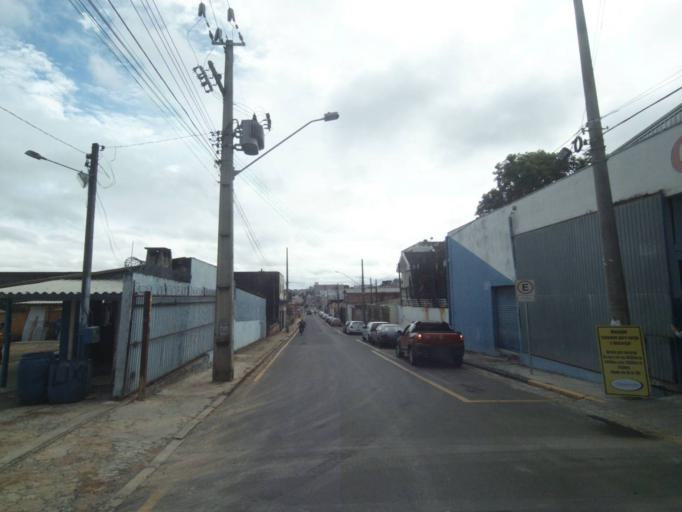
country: BR
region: Parana
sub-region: Telemaco Borba
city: Telemaco Borba
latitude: -24.3264
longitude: -50.6250
